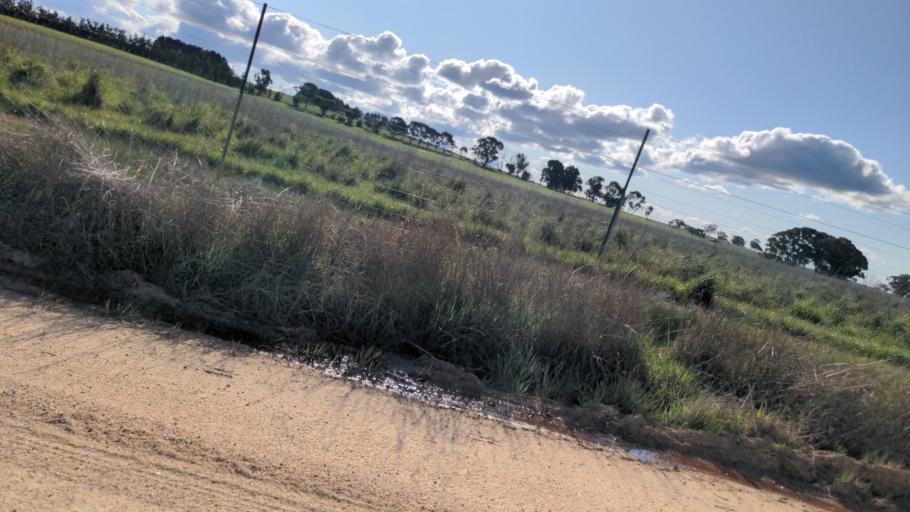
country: AU
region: New South Wales
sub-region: Blayney
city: Millthorpe
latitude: -33.4139
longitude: 149.3016
